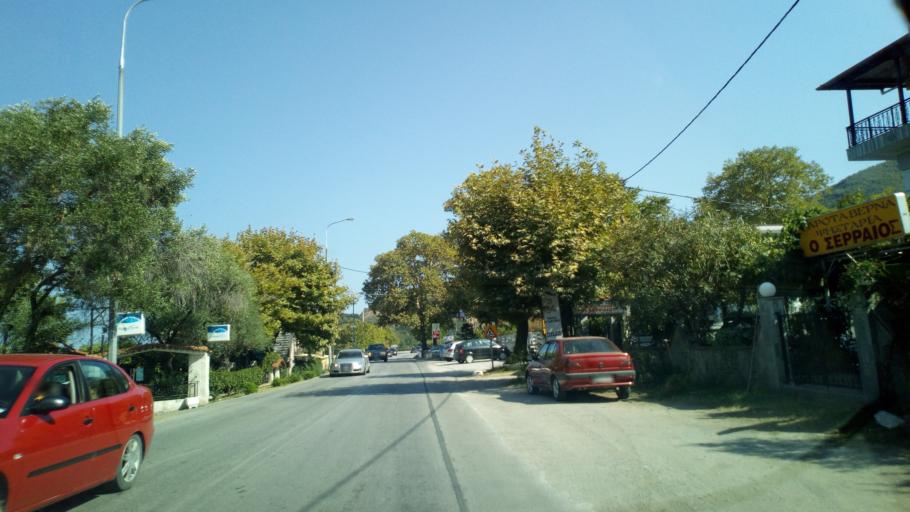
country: GR
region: Central Macedonia
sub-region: Nomos Thessalonikis
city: Stavros
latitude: 40.6604
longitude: 23.7247
